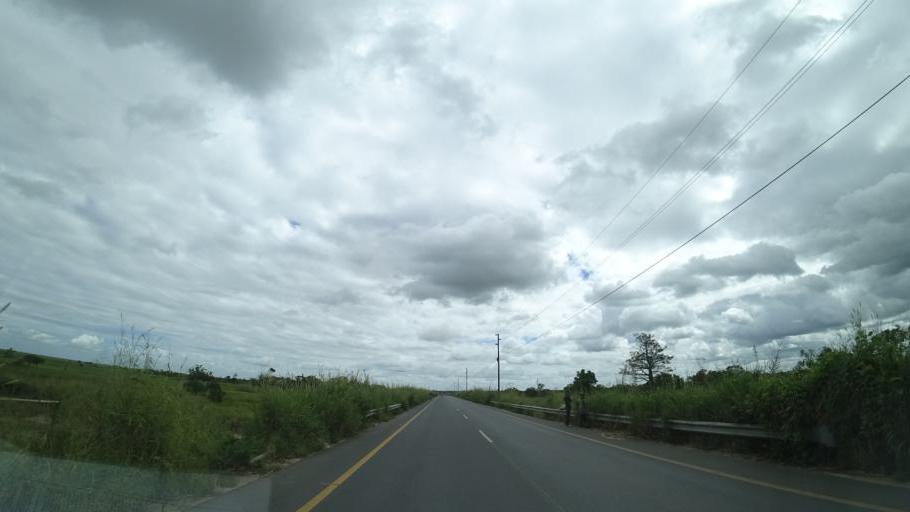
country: MZ
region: Sofala
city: Dondo
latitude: -19.5217
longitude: 34.6226
